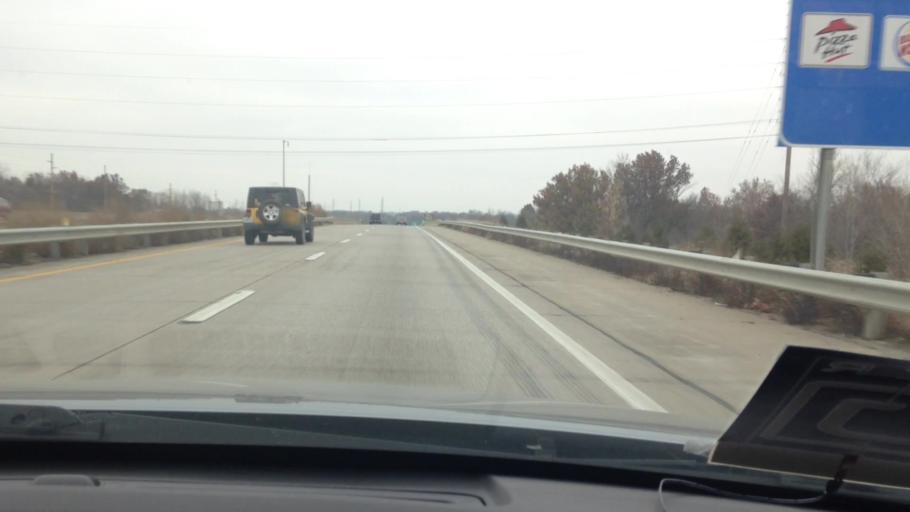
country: US
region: Missouri
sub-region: Cass County
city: Harrisonville
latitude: 38.6445
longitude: -94.3609
